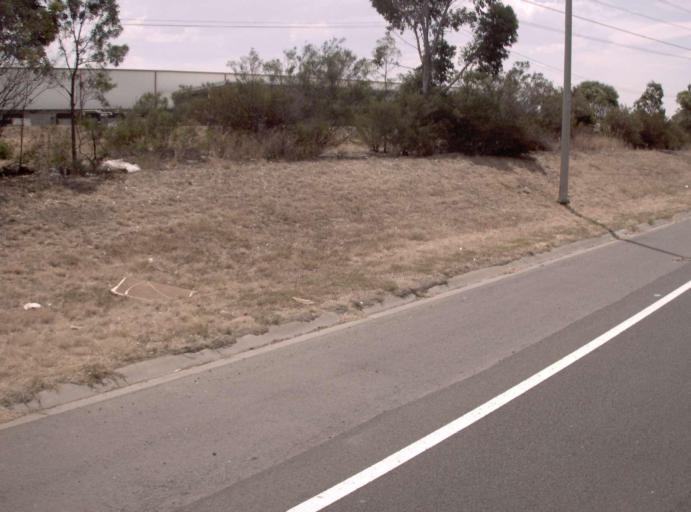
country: AU
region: Victoria
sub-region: Brimbank
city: Sunshine West
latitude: -37.8069
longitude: 144.8075
